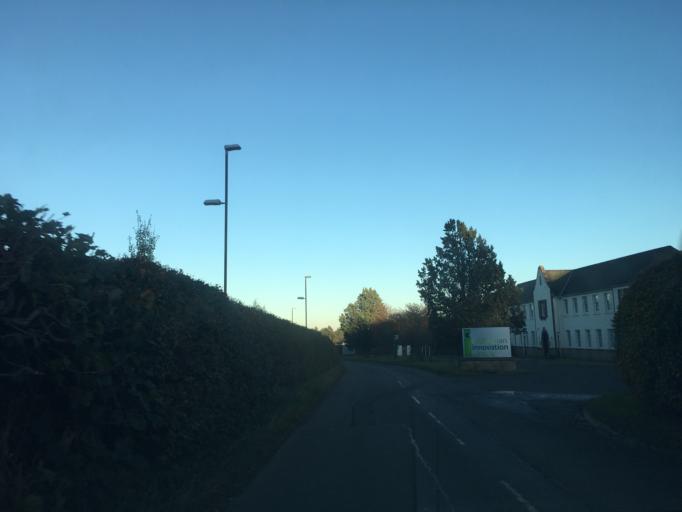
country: GB
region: Scotland
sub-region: Midlothian
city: Loanhead
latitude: 55.8682
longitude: -3.1959
